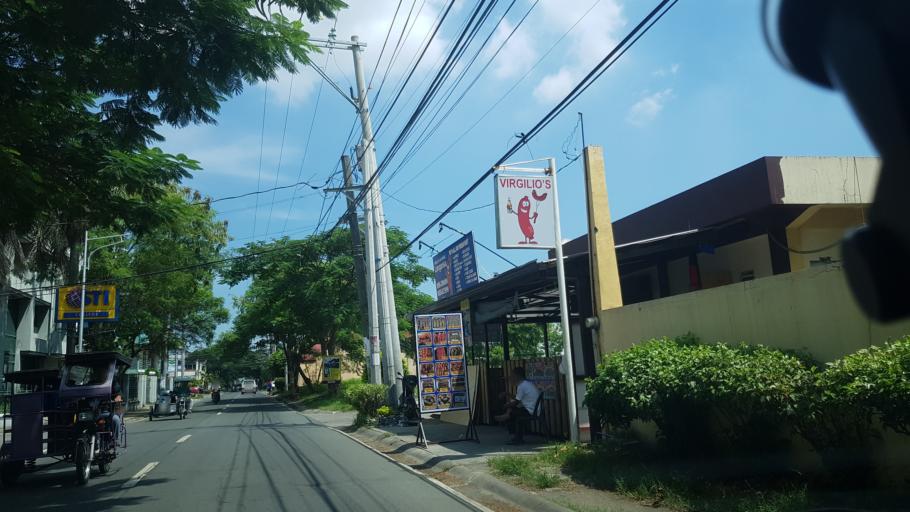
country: PH
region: Calabarzon
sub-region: Province of Rizal
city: Las Pinas
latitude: 14.4305
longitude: 120.9944
